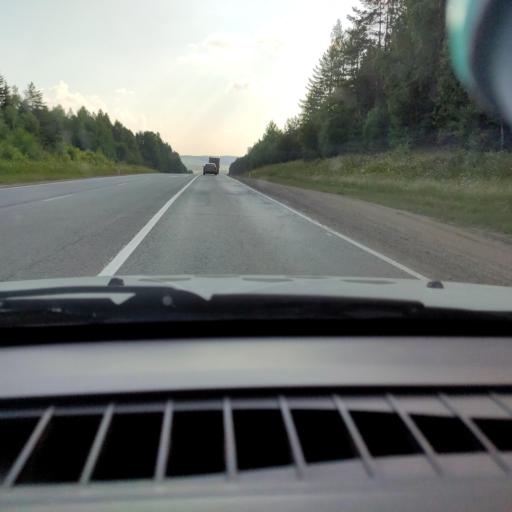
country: RU
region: Perm
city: Nytva
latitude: 57.9602
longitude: 55.1642
